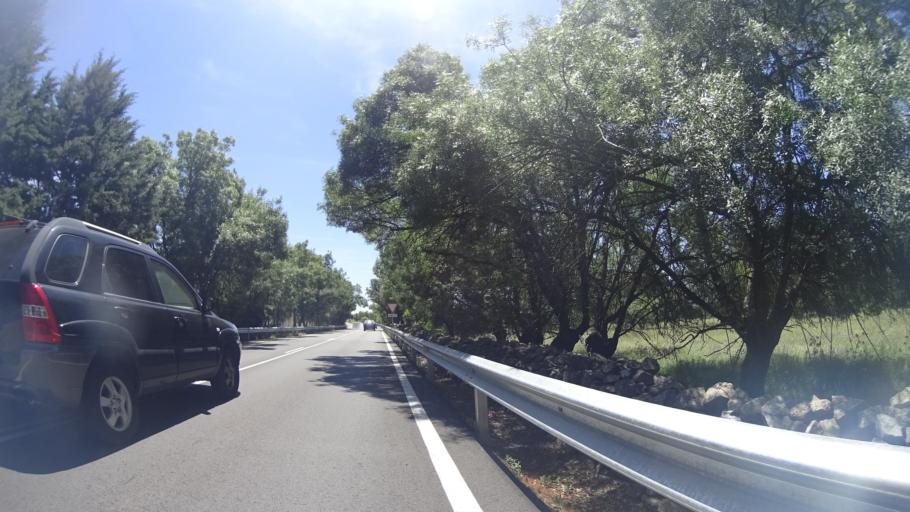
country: ES
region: Madrid
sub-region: Provincia de Madrid
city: Galapagar
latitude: 40.5937
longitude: -4.0133
